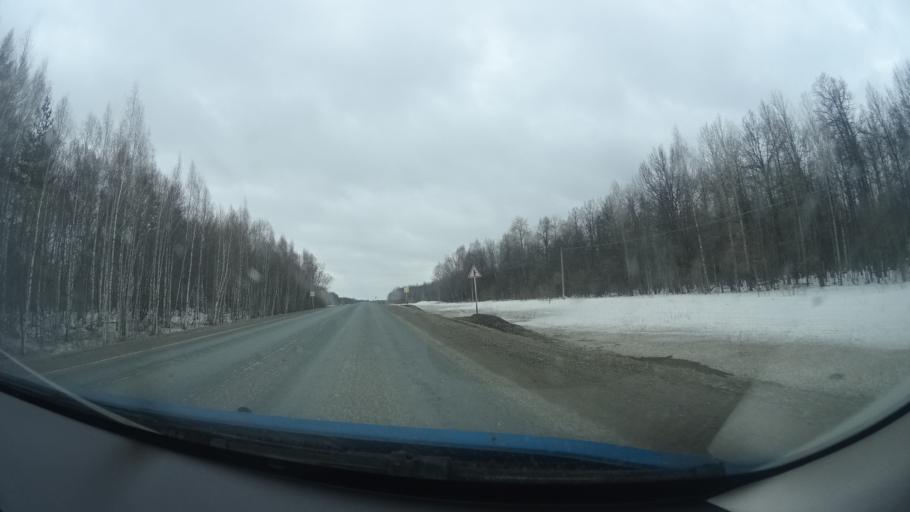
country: RU
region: Bashkortostan
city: Birsk
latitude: 55.3185
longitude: 55.6193
